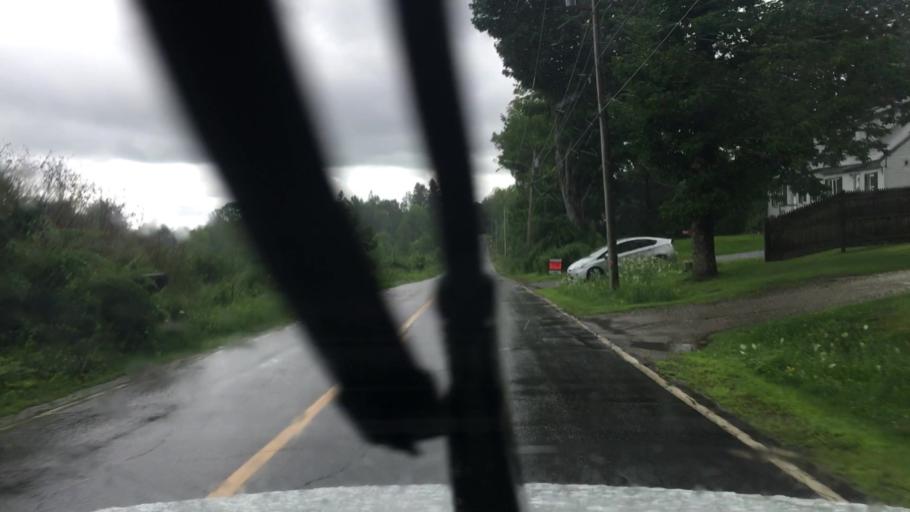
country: US
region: Maine
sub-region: Kennebec County
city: Winthrop
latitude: 44.3101
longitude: -69.9242
